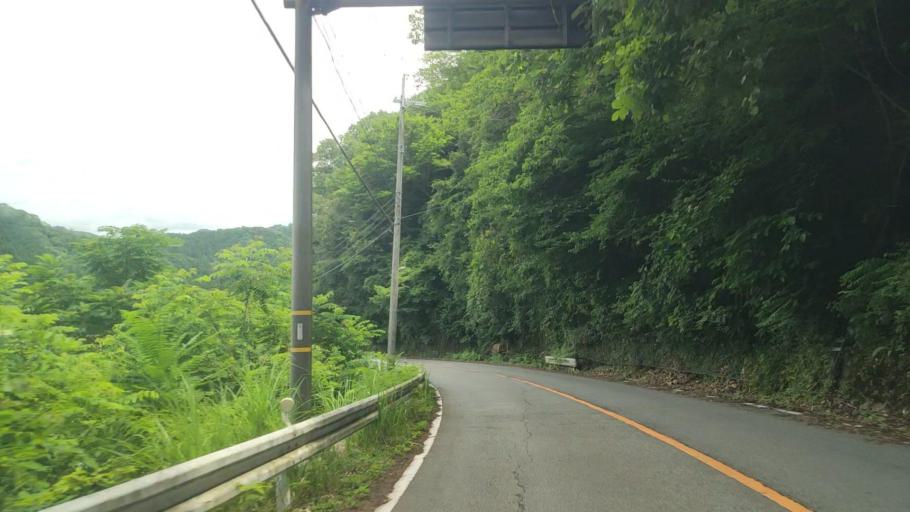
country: JP
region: Hyogo
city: Yamazakicho-nakabirose
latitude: 35.1048
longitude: 134.3603
